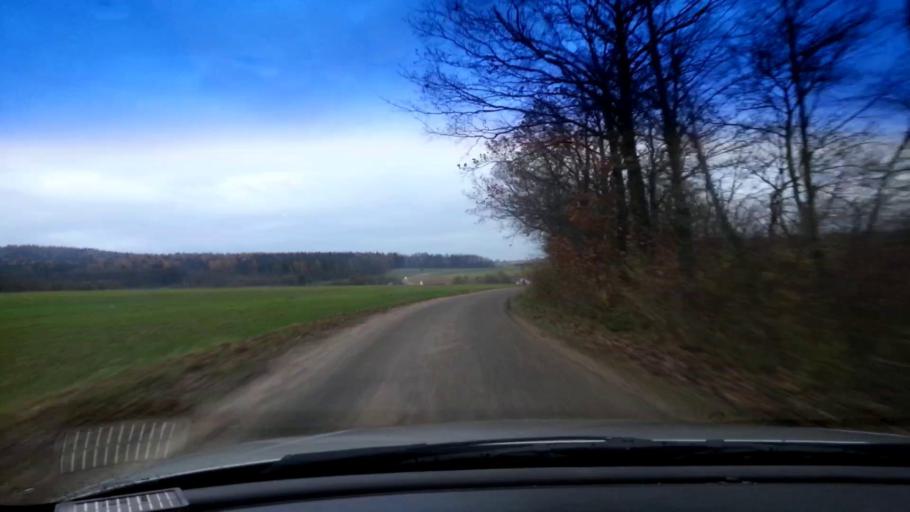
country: DE
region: Bavaria
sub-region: Upper Franconia
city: Litzendorf
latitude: 49.9422
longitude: 11.0118
